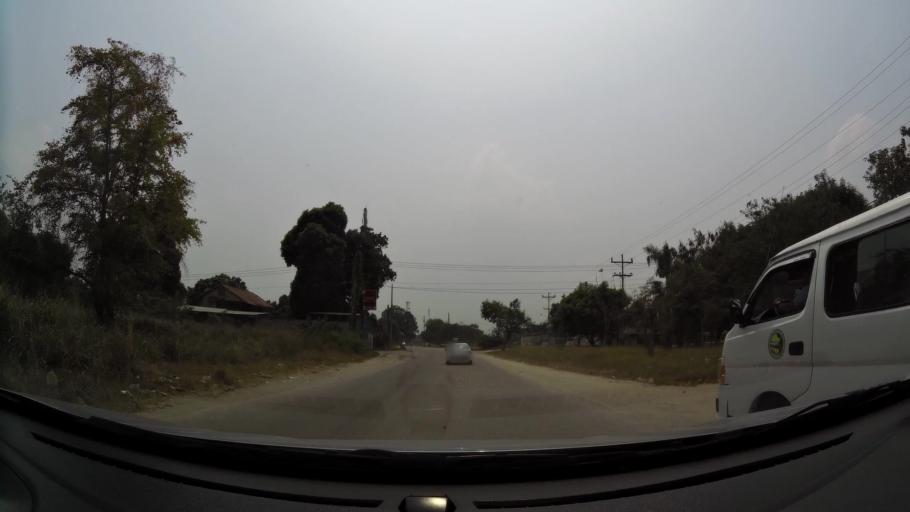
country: HN
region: Cortes
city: La Lima
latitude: 15.4366
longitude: -87.9085
